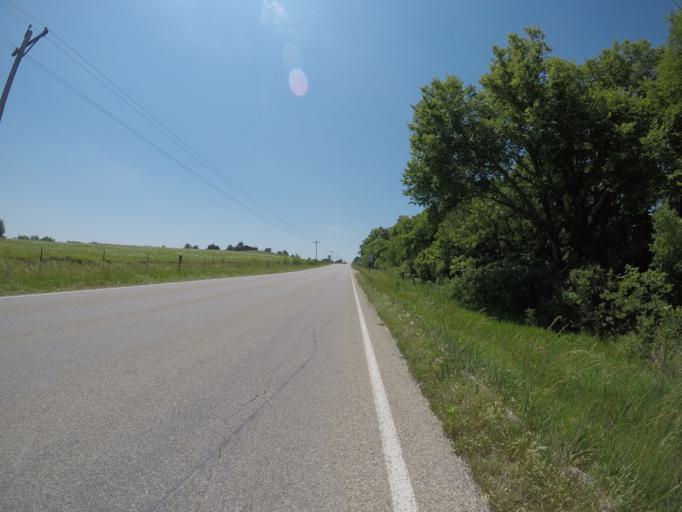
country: US
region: Kansas
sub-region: Pottawatomie County
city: Westmoreland
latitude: 39.2657
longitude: -96.4450
